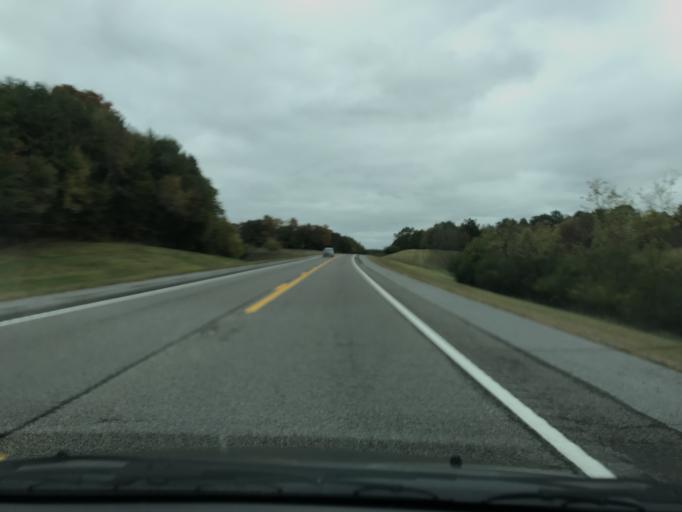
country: US
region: Tennessee
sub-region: Rhea County
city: Graysville
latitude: 35.4294
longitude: -85.0251
